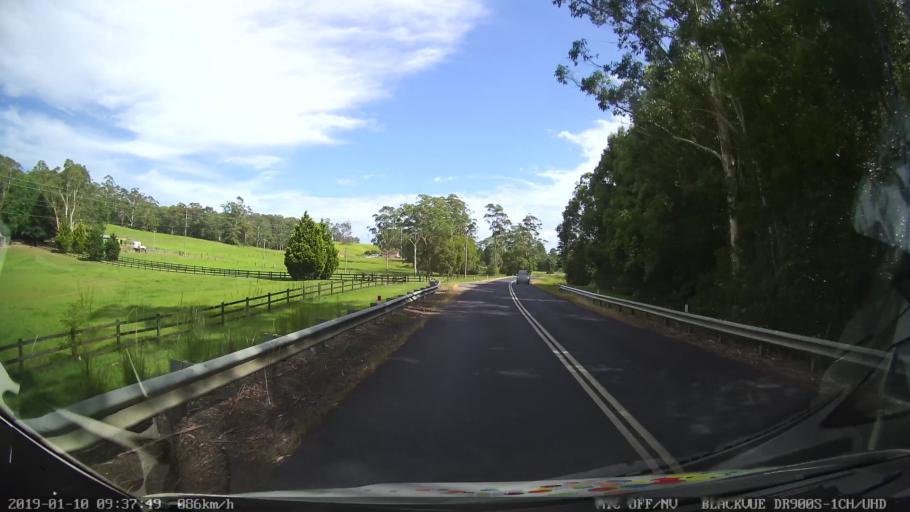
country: AU
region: New South Wales
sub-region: Coffs Harbour
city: Nana Glen
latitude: -30.1835
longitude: 153.0067
